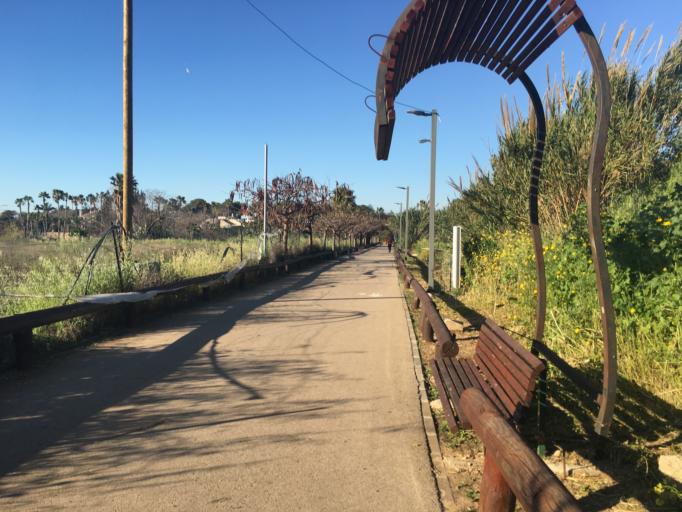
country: IL
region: Tel Aviv
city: Ramat HaSharon
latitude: 32.1462
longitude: 34.8274
